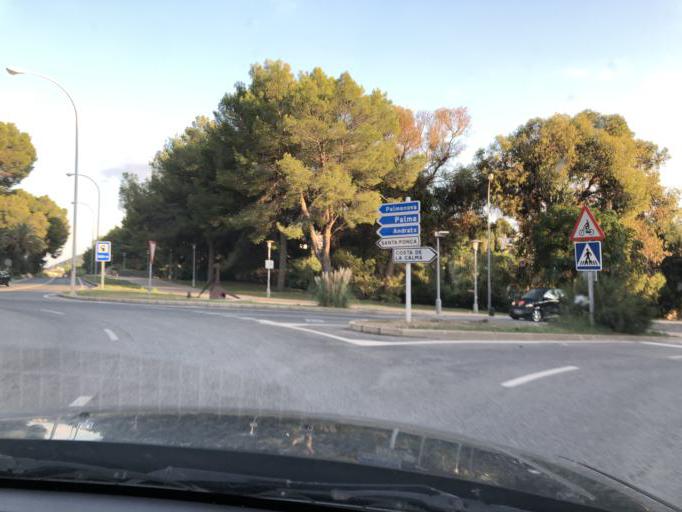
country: ES
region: Balearic Islands
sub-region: Illes Balears
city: Santa Ponsa
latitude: 39.5276
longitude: 2.4824
